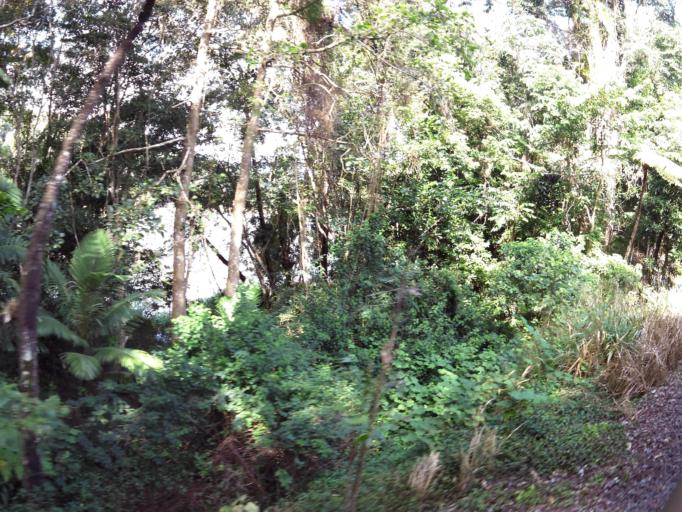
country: AU
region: Queensland
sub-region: Tablelands
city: Kuranda
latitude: -16.8298
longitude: 145.6382
